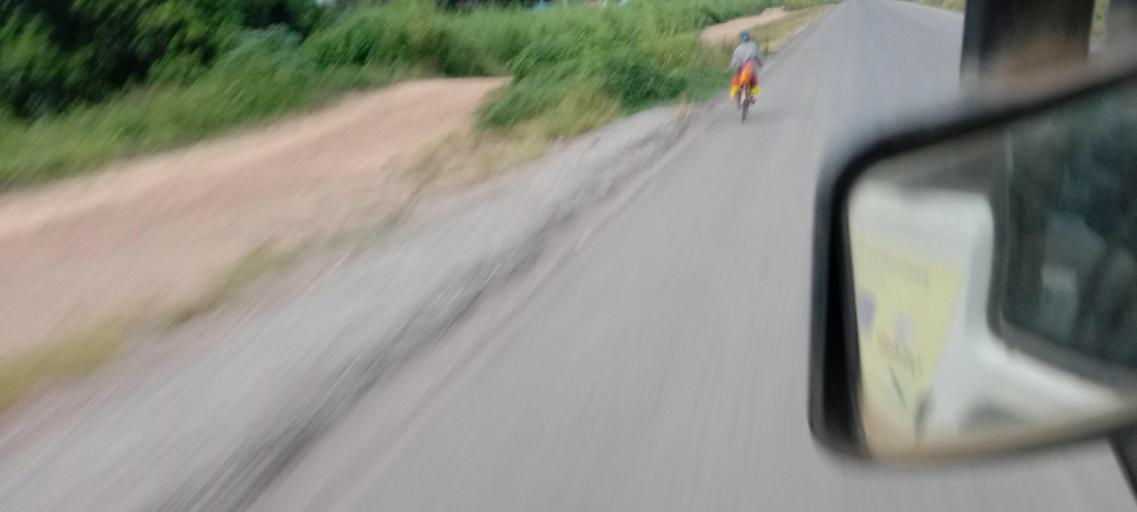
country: TZ
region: Morogoro
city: Ifakara
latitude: -7.9600
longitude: 36.8518
